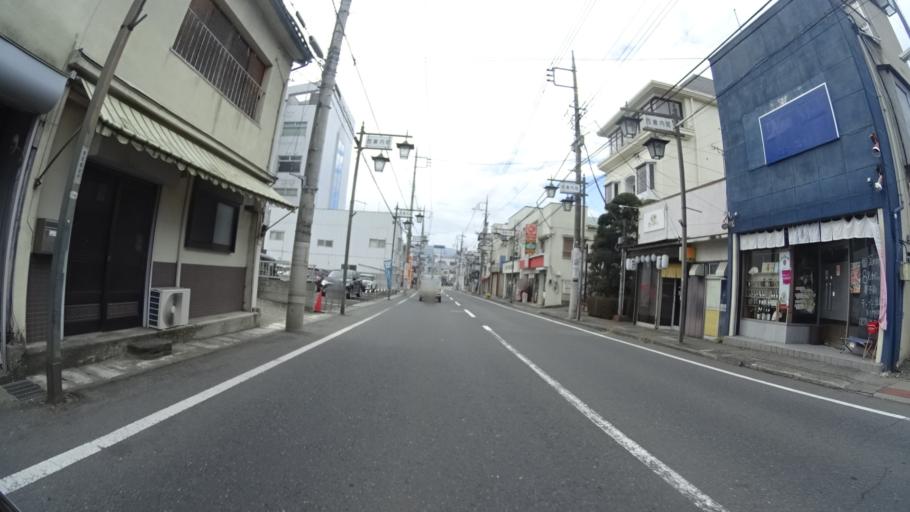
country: JP
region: Gunma
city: Numata
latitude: 36.6452
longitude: 139.0433
